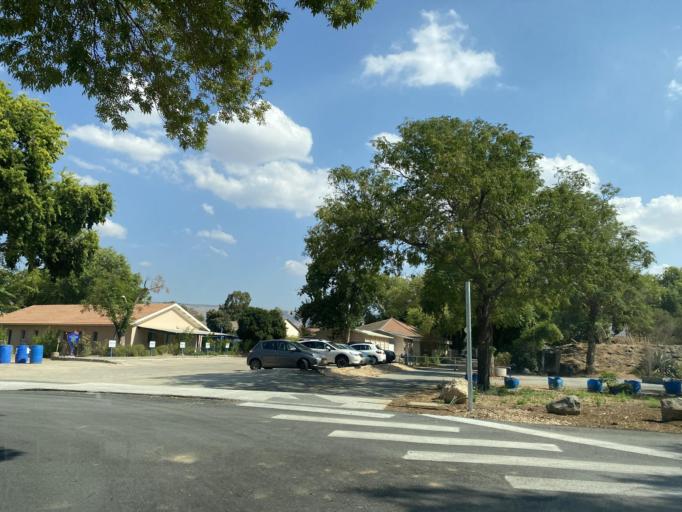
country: IL
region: Northern District
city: Qiryat Shemona
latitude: 33.1713
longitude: 35.6102
